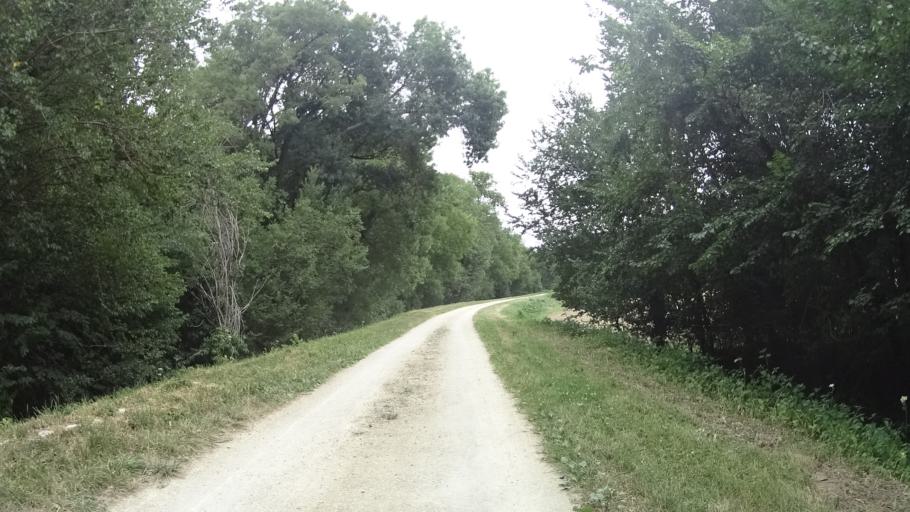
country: FR
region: Centre
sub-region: Departement d'Indre-et-Loire
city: Huismes
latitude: 47.2575
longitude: 0.2660
